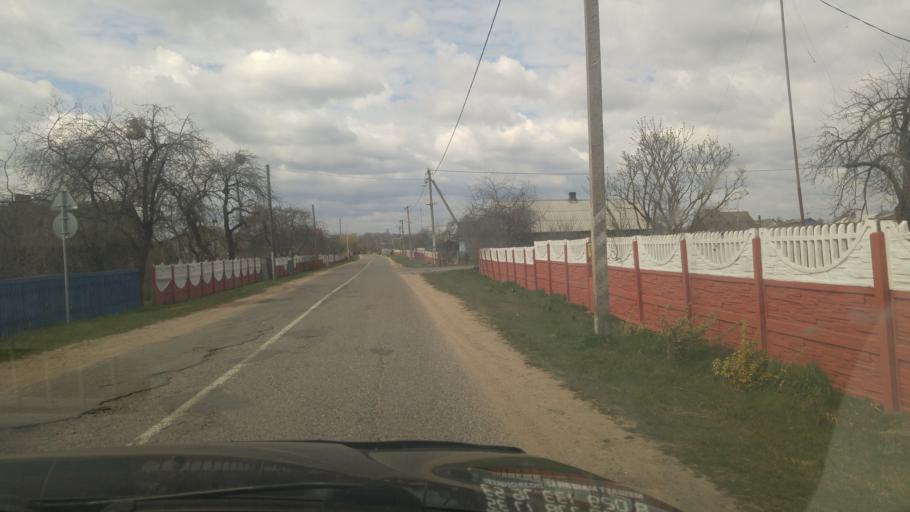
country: BY
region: Minsk
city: Pukhavichy
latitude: 53.4162
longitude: 28.2694
